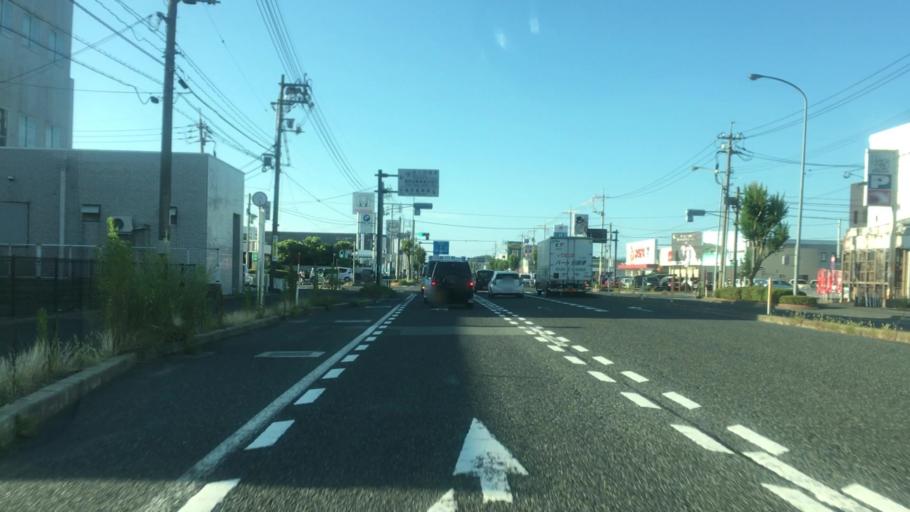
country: JP
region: Tottori
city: Tottori
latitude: 35.5160
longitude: 134.2021
